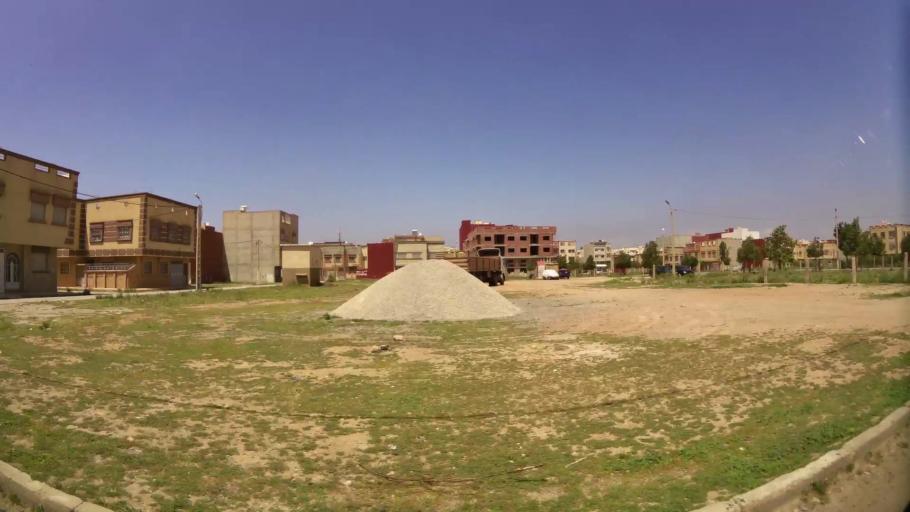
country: MA
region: Oriental
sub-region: Oujda-Angad
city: Oujda
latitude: 34.6949
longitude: -1.8881
